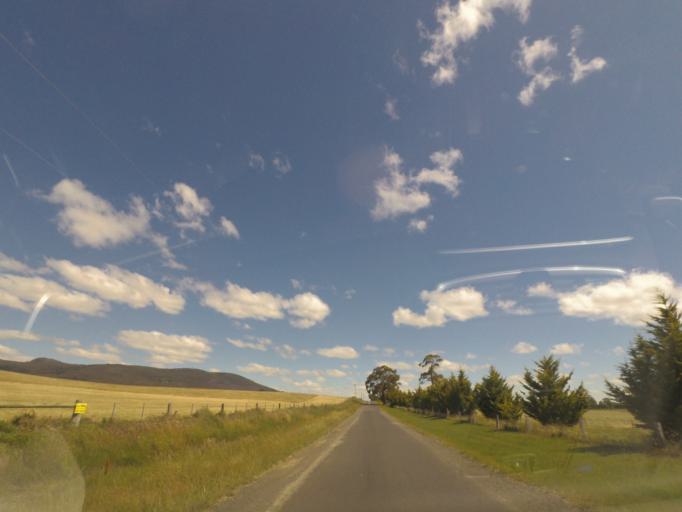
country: AU
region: Victoria
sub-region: Hume
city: Sunbury
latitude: -37.3293
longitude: 144.5593
